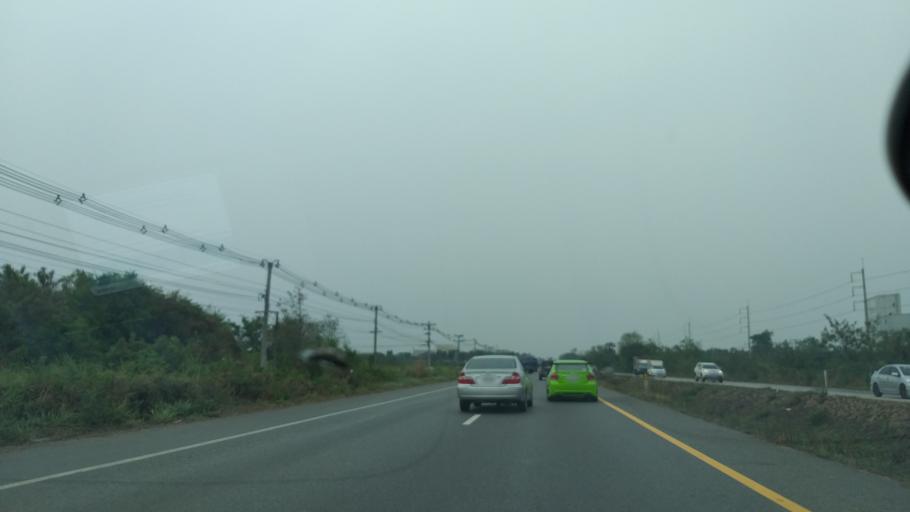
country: TH
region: Chon Buri
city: Ko Chan
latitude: 13.3387
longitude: 101.2705
